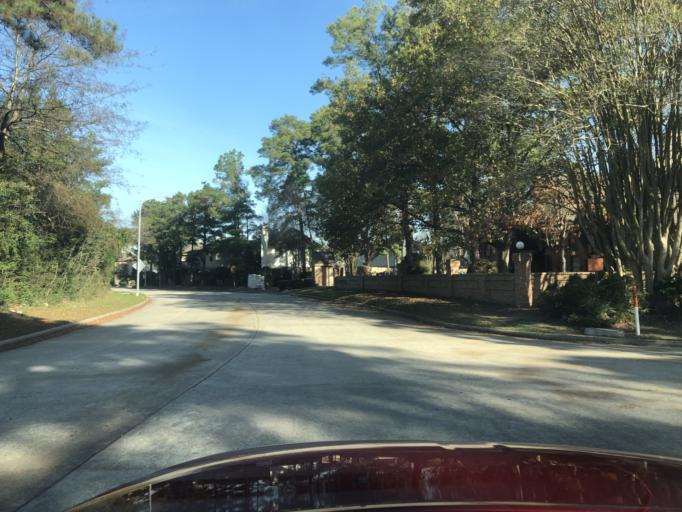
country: US
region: Texas
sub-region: Harris County
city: Spring
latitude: 30.0049
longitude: -95.4566
